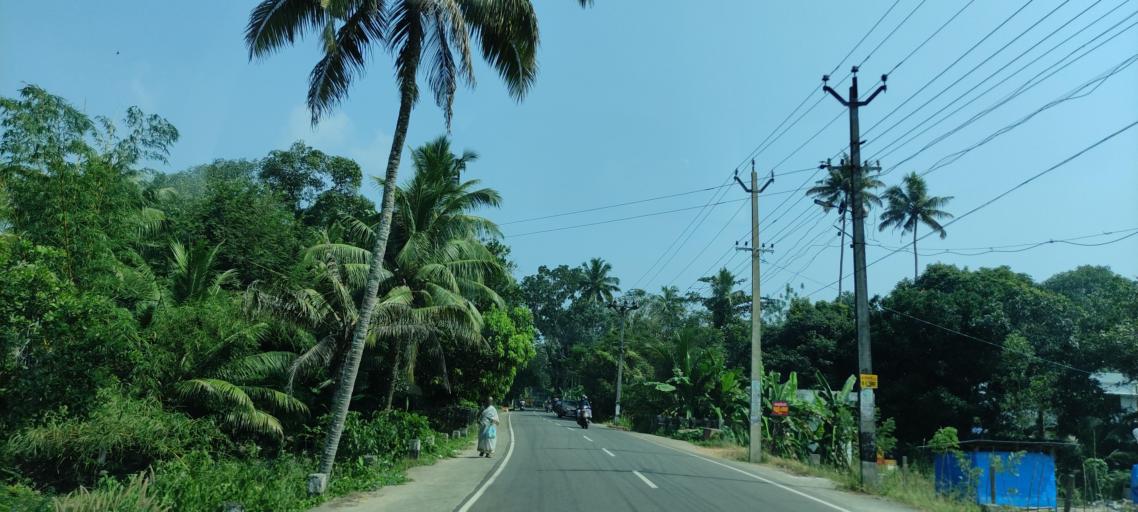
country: IN
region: Kerala
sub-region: Alappuzha
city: Shertallai
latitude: 9.6018
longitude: 76.3118
